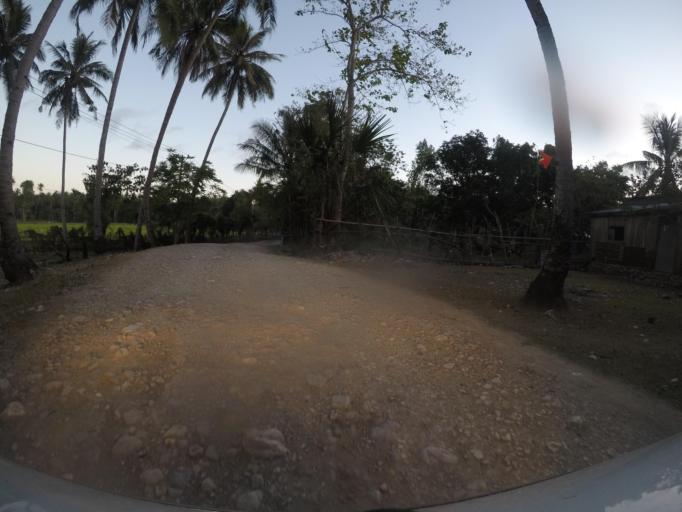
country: TL
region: Viqueque
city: Viqueque
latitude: -8.7782
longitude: 126.6368
